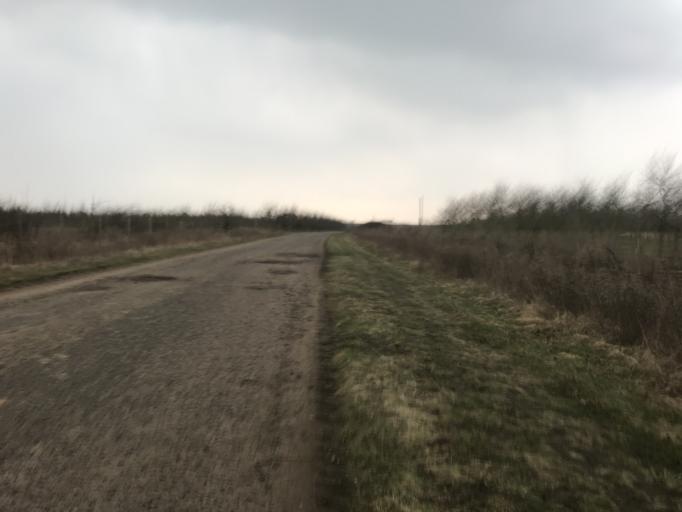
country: DE
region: Rheinland-Pfalz
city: Essenheim
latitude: 49.9611
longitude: 8.1511
